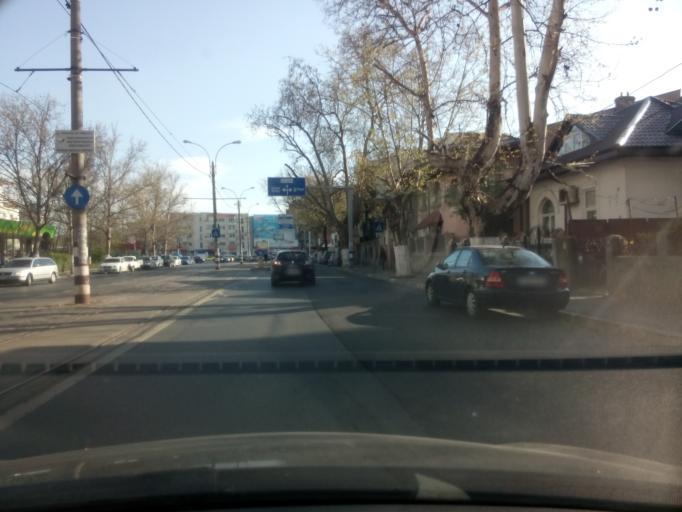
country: RO
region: Bucuresti
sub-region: Municipiul Bucuresti
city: Bucharest
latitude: 44.4547
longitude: 26.1051
